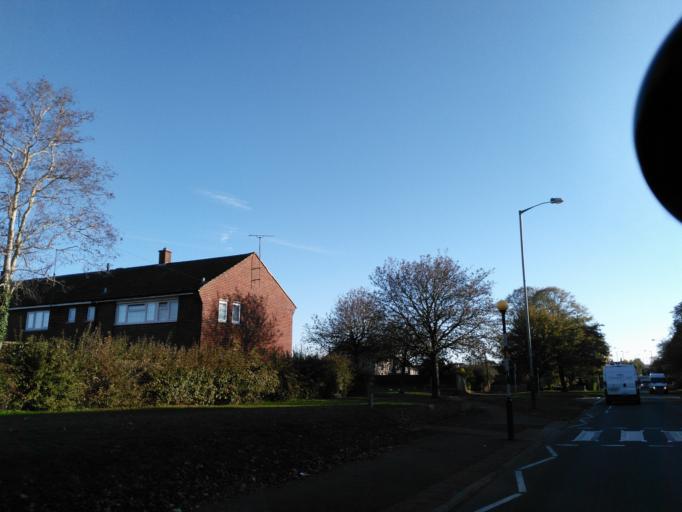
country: GB
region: England
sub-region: Wiltshire
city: Chippenham
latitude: 51.4627
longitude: -2.1380
